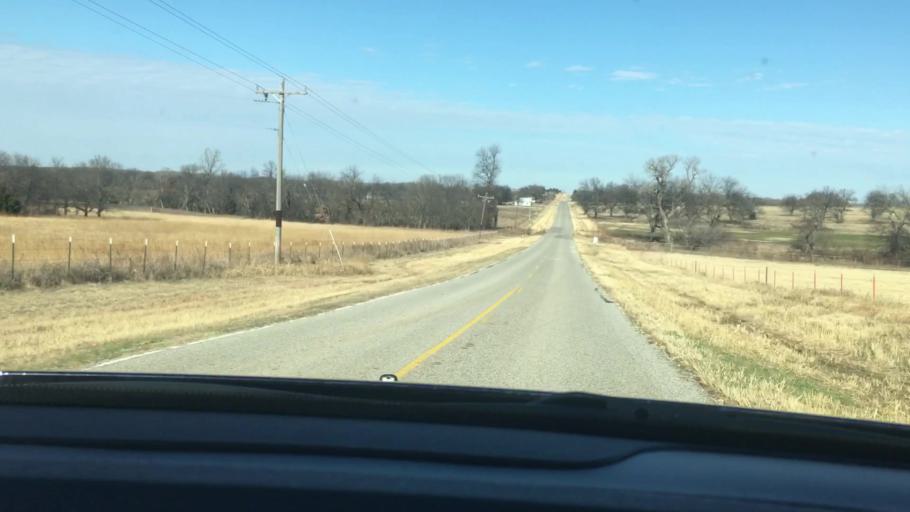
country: US
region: Oklahoma
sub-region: Garvin County
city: Wynnewood
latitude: 34.6749
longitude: -97.1254
